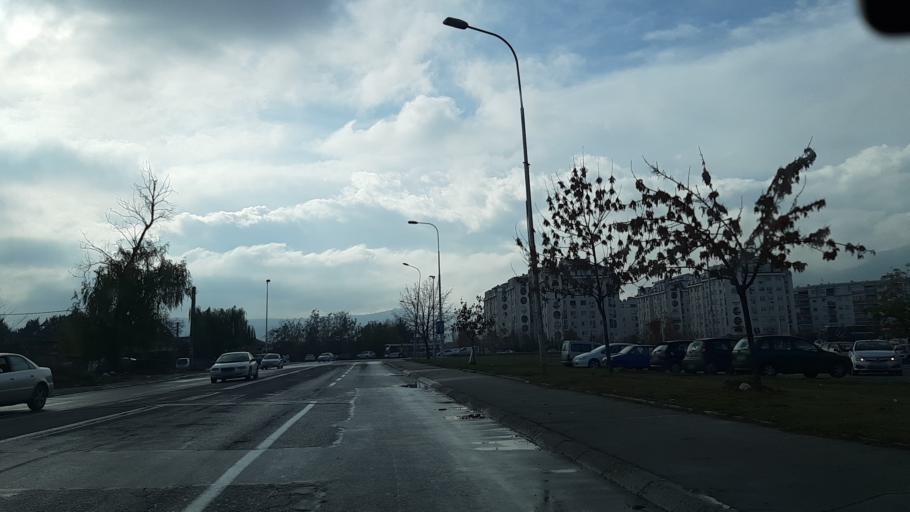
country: MK
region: Kisela Voda
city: Usje
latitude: 41.9804
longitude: 21.4795
